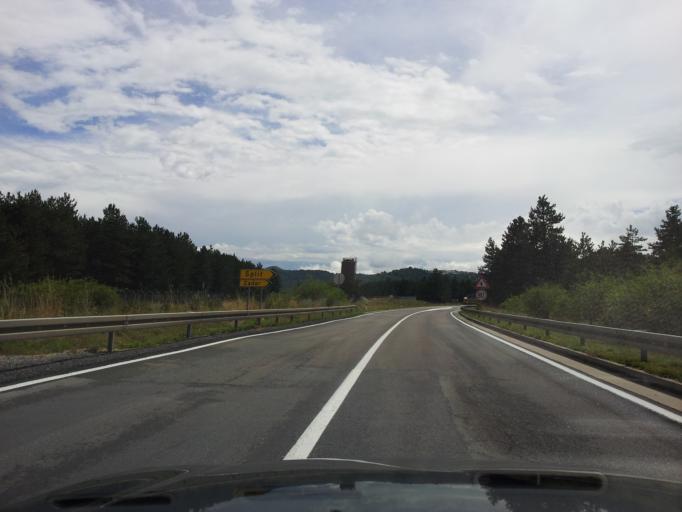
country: HR
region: Zadarska
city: Gracac
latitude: 44.5545
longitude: 15.7608
